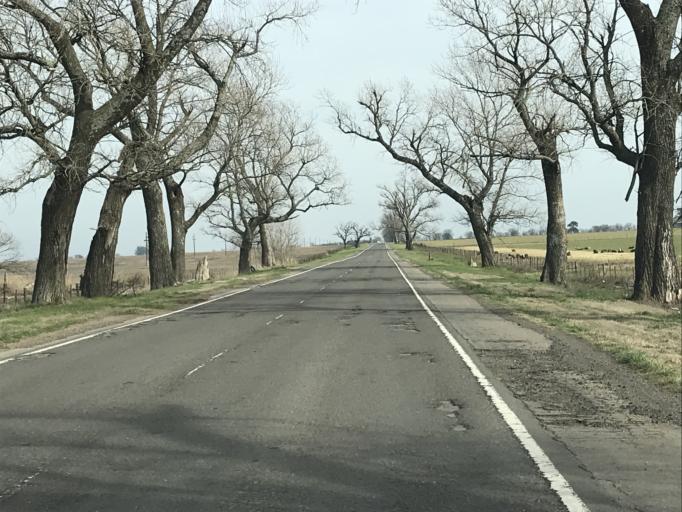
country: AR
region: Santa Fe
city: Armstrong
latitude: -32.7605
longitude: -61.6840
